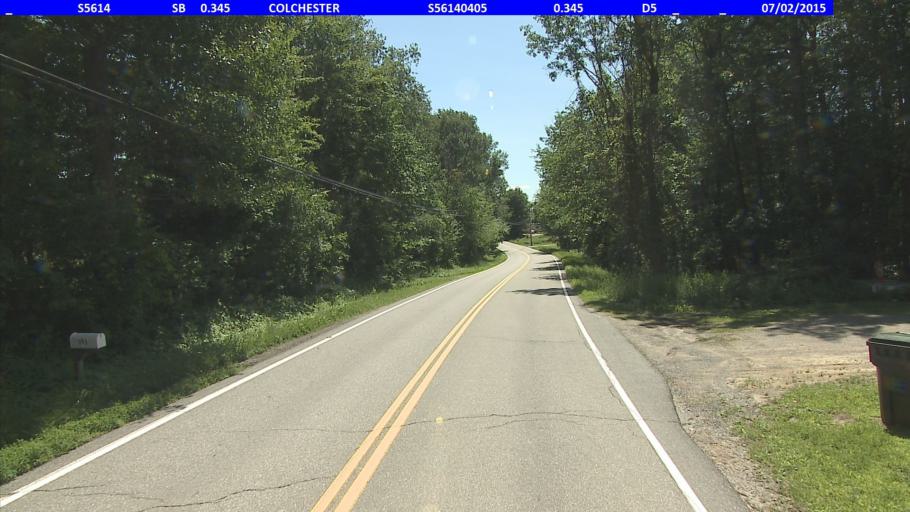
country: US
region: Vermont
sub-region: Chittenden County
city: Colchester
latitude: 44.5270
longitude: -73.1519
